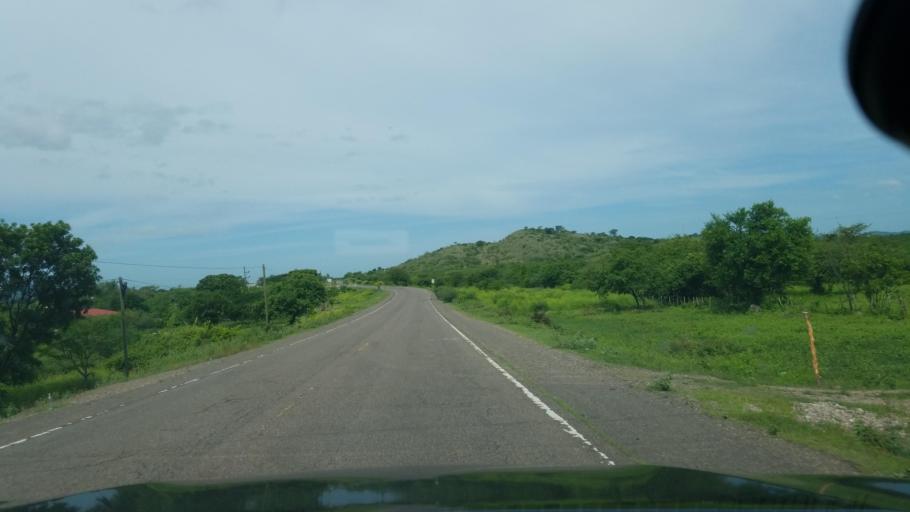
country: HN
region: Choluteca
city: Santa Ana de Yusguare
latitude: 13.3576
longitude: -87.0978
